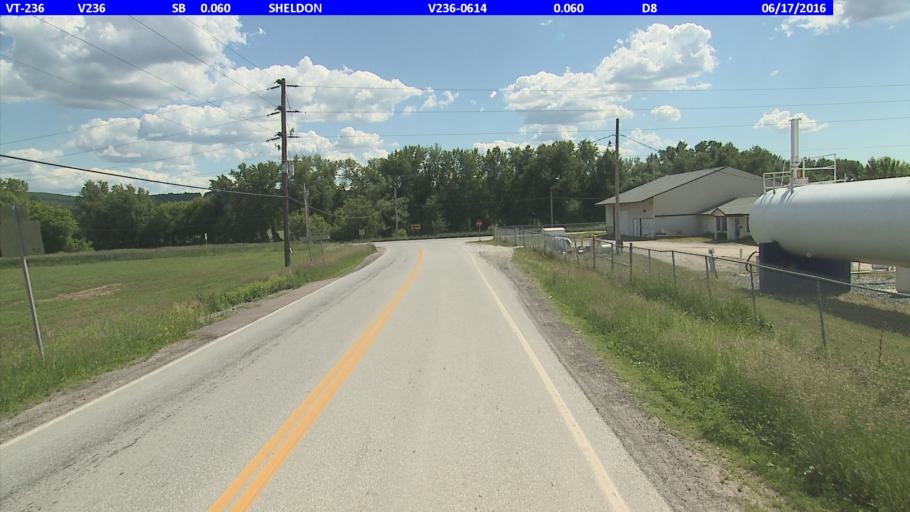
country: US
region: Vermont
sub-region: Franklin County
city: Enosburg Falls
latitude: 44.9119
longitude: -72.8655
